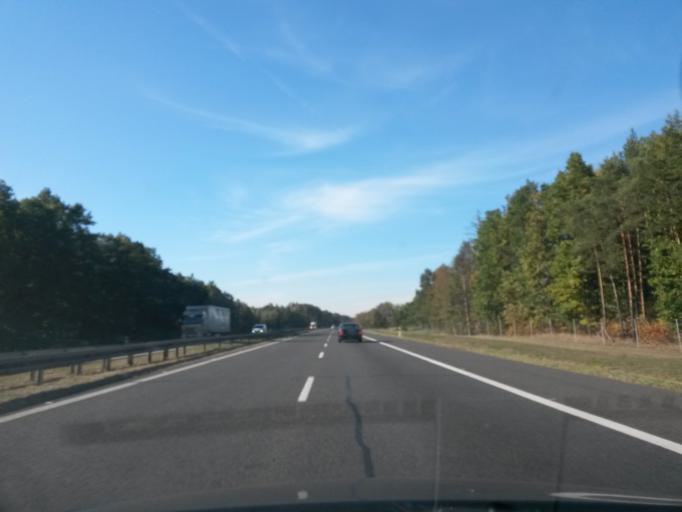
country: PL
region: Opole Voivodeship
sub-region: Powiat opolski
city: Niemodlin
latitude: 50.6860
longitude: 17.6381
